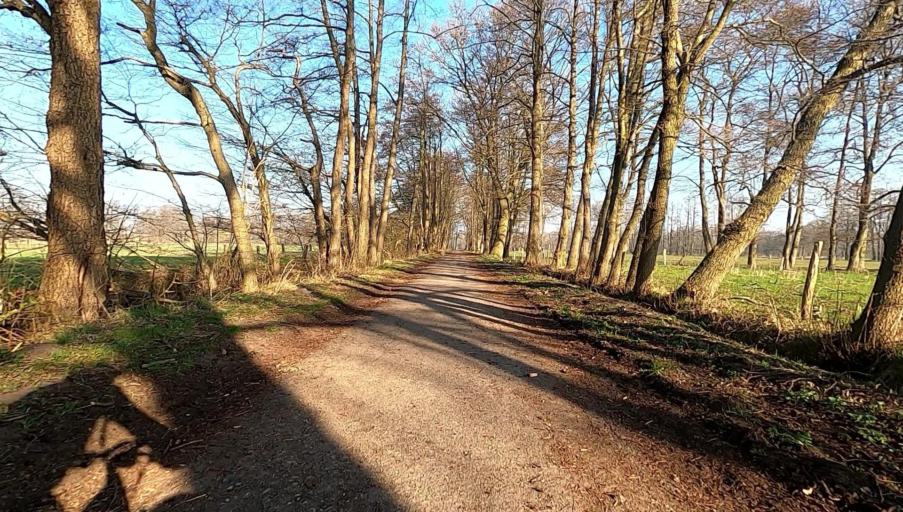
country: DE
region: Lower Saxony
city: Garbsen-Mitte
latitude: 52.4573
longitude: 9.6397
